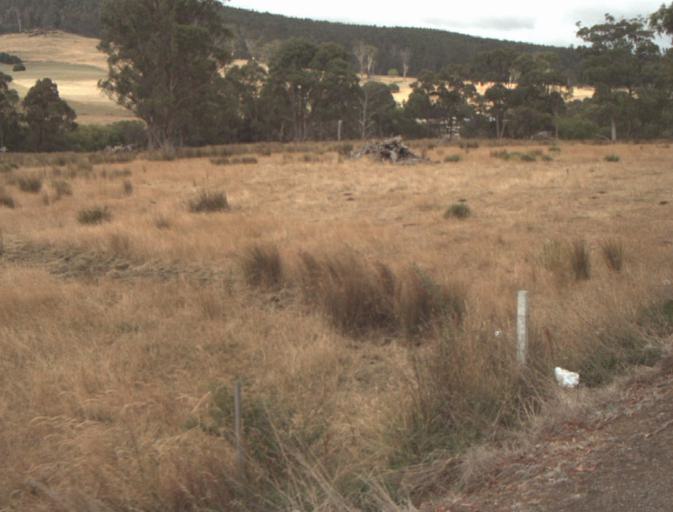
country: AU
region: Tasmania
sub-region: Dorset
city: Scottsdale
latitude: -41.4679
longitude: 147.5779
